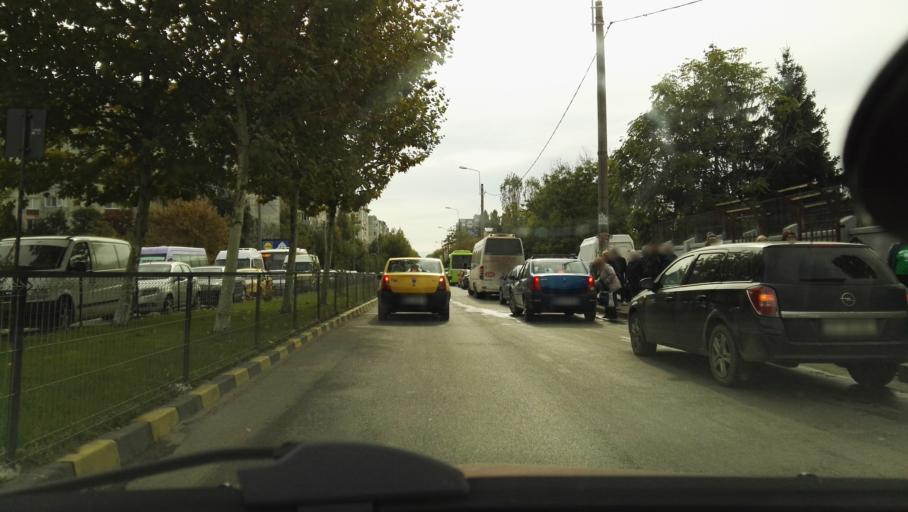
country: RO
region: Bucuresti
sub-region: Municipiul Bucuresti
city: Bucharest
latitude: 44.3926
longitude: 26.1226
